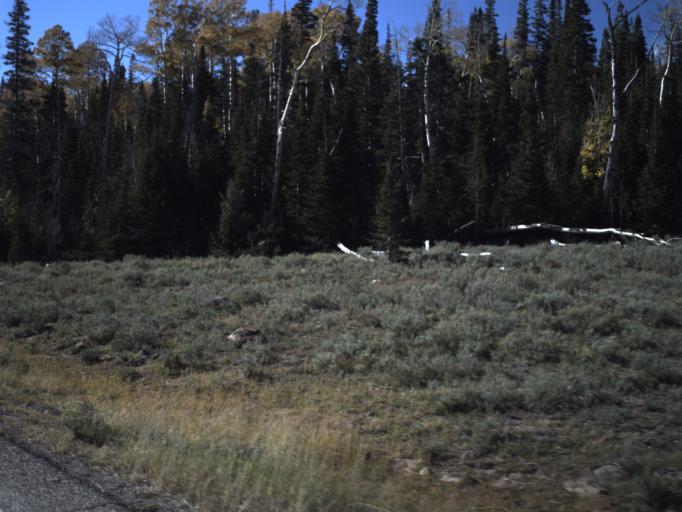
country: US
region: Utah
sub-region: Iron County
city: Parowan
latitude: 37.6588
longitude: -112.7454
